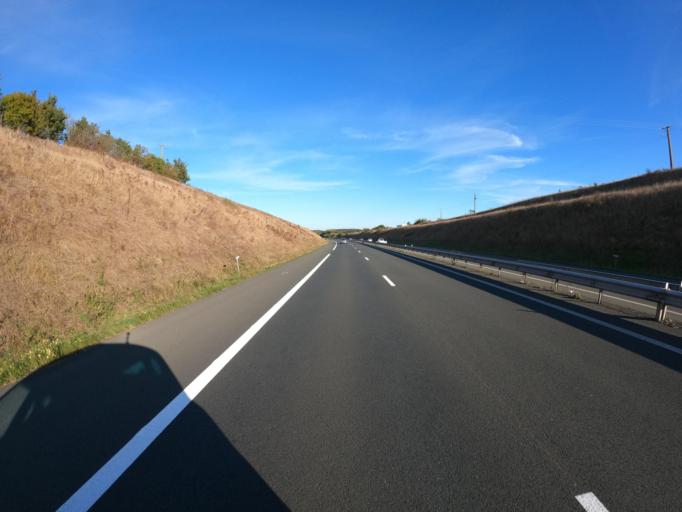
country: FR
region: Pays de la Loire
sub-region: Departement de Maine-et-Loire
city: Chemille-Melay
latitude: 47.2446
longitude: -0.6804
